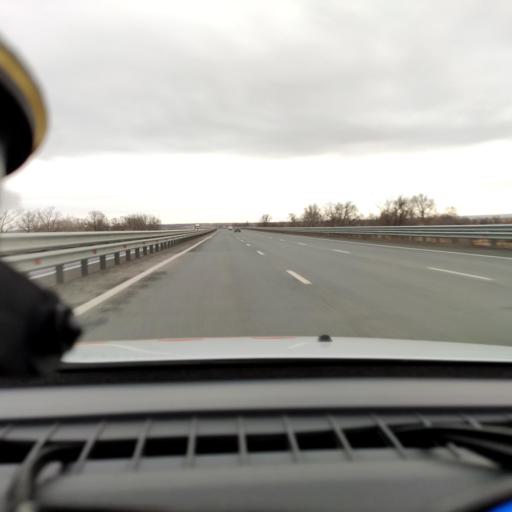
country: RU
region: Samara
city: Smyshlyayevka
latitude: 53.1713
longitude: 50.3146
